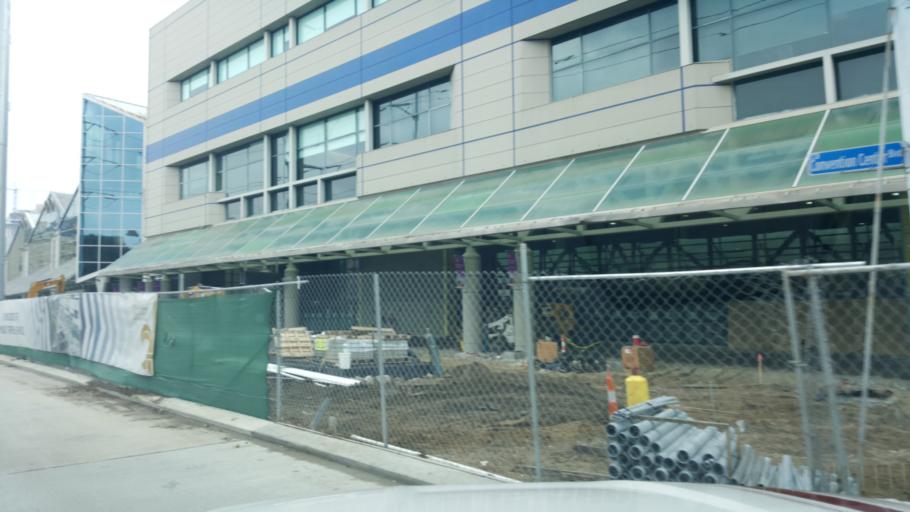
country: US
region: Louisiana
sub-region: Orleans Parish
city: New Orleans
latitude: 29.9407
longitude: -90.0645
